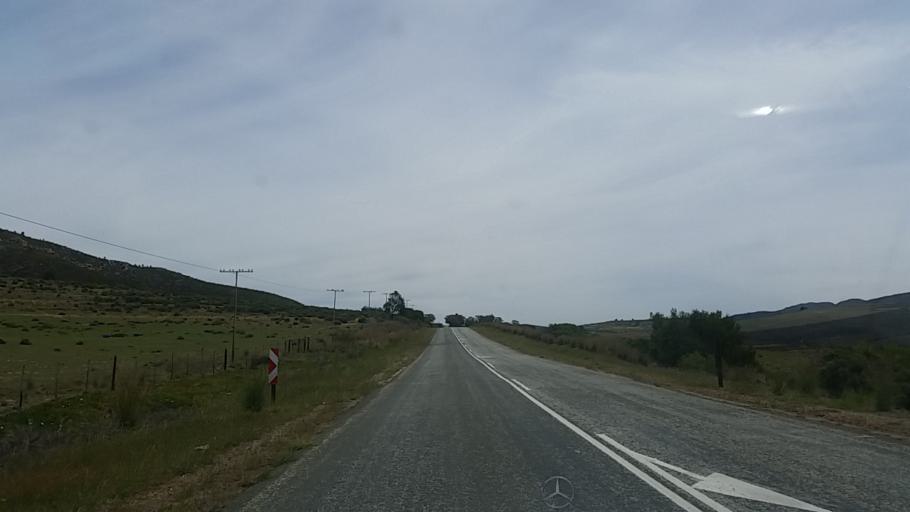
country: ZA
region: Western Cape
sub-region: Eden District Municipality
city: Knysna
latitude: -33.7726
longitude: 22.9368
